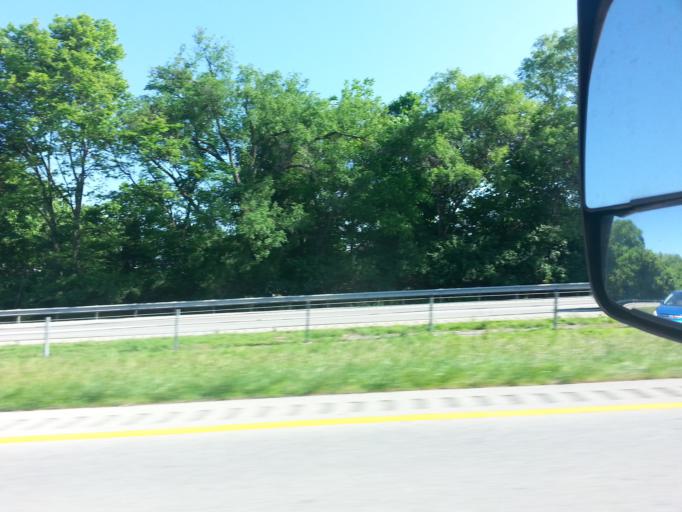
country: US
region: Kentucky
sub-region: Jefferson County
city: Saint Matthews
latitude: 38.2359
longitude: -85.6461
